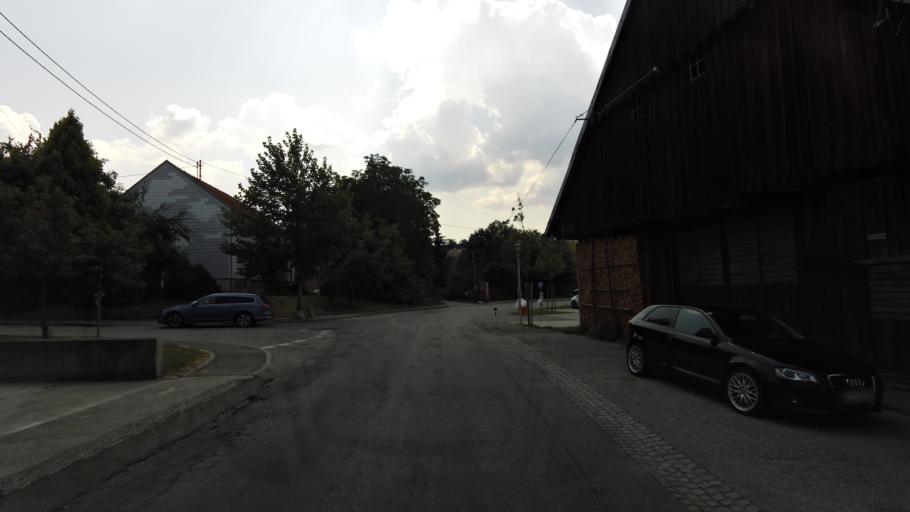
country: AT
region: Upper Austria
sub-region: Politischer Bezirk Ried im Innkreis
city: Waldzell
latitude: 48.1347
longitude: 13.4271
